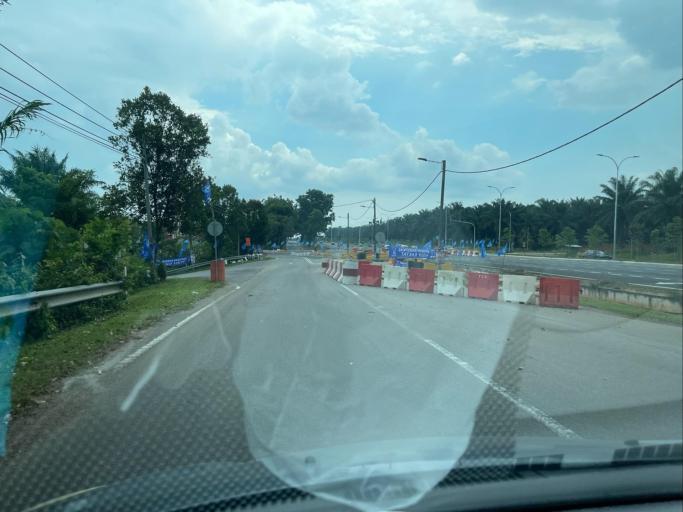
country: MY
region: Melaka
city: Kampung Ayer Keroh
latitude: 2.3189
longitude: 102.2491
